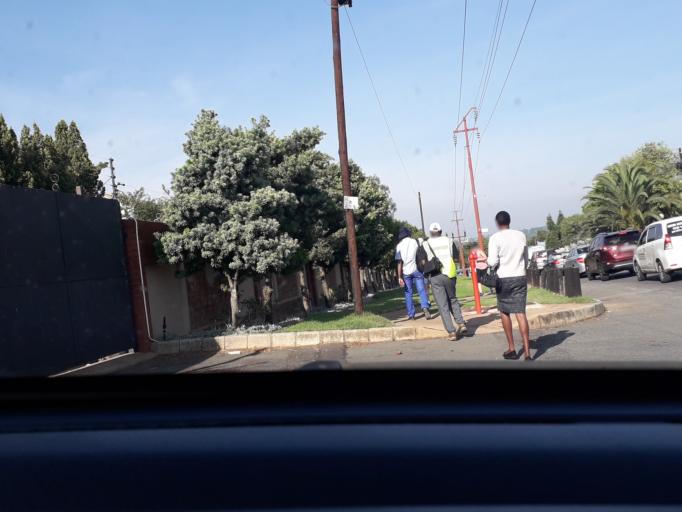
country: ZA
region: Gauteng
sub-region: City of Johannesburg Metropolitan Municipality
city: Midrand
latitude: -26.0667
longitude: 28.0573
